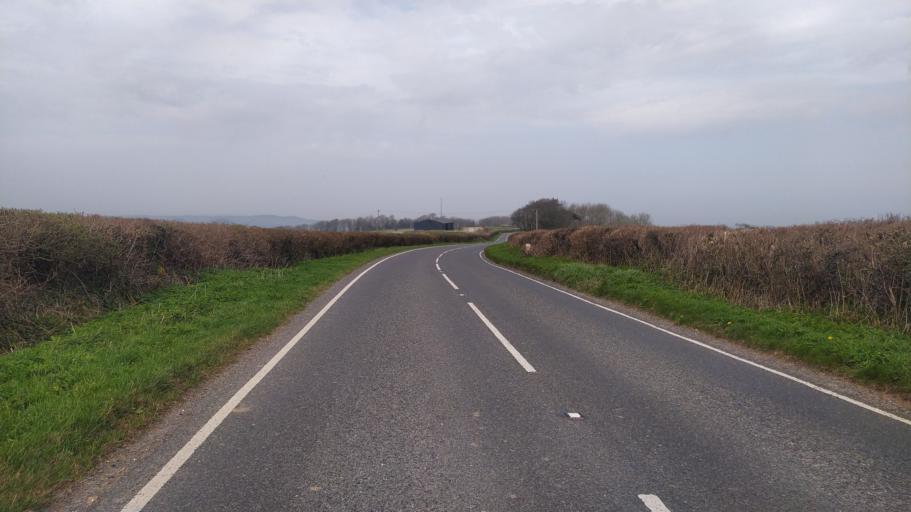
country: GB
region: England
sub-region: Dorset
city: Beaminster
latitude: 50.8432
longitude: -2.7130
